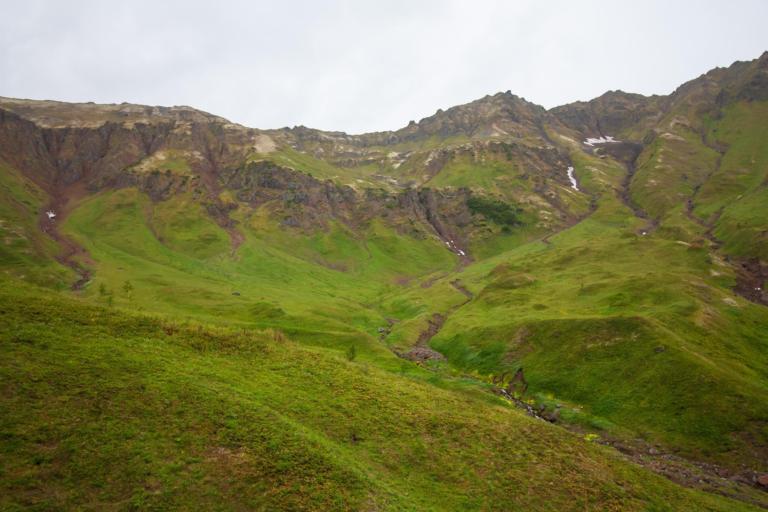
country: RU
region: Kamtsjatka
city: Yelizovo
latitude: 54.0198
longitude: 158.0816
